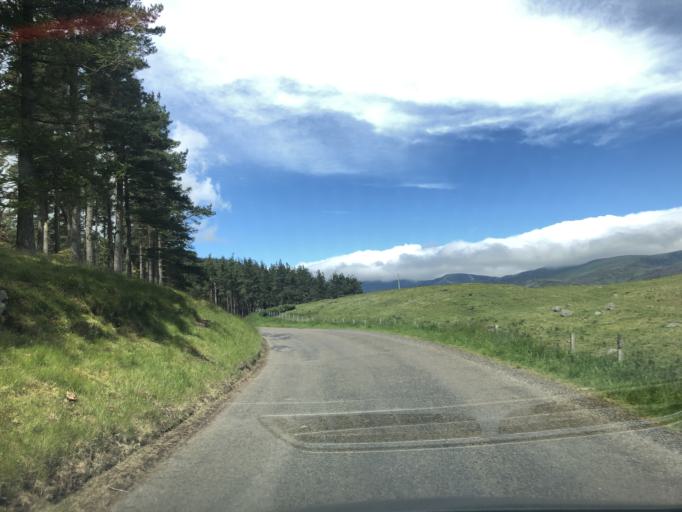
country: GB
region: Scotland
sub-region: Angus
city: Kirriemuir
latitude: 56.8110
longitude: -3.0523
